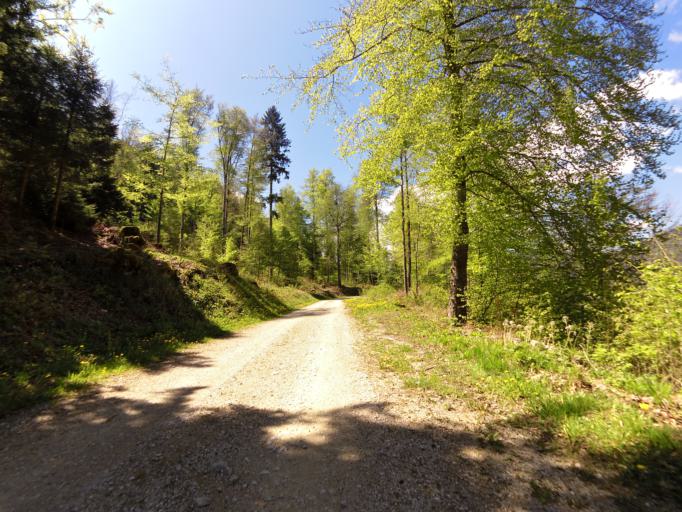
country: CH
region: Vaud
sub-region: Jura-Nord vaudois District
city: Vallorbe
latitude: 46.7041
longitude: 6.3686
